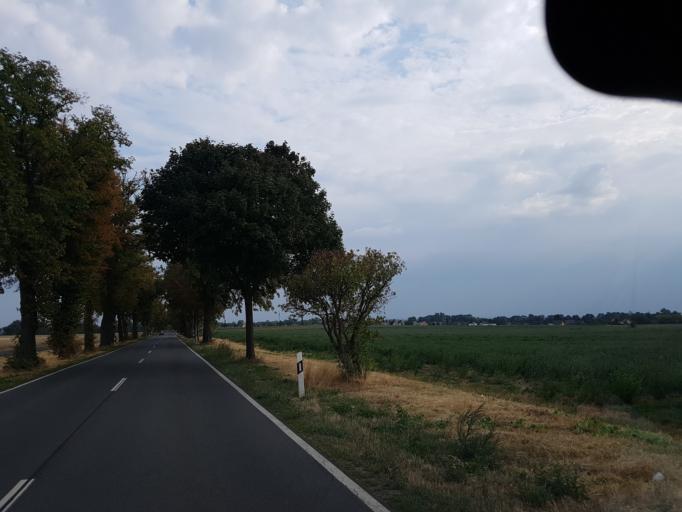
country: DE
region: Saxony-Anhalt
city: Wittenburg
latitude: 51.8883
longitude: 12.6250
